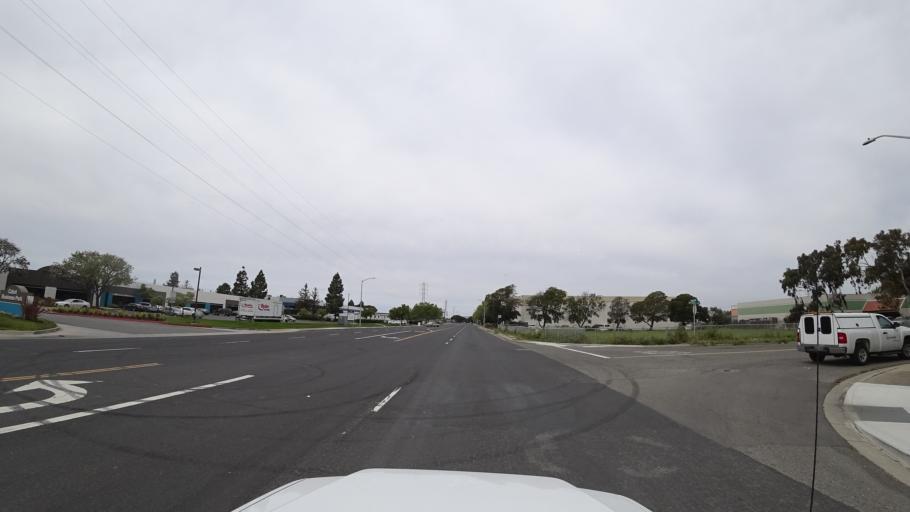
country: US
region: California
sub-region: Alameda County
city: San Lorenzo
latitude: 37.6396
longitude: -122.1337
